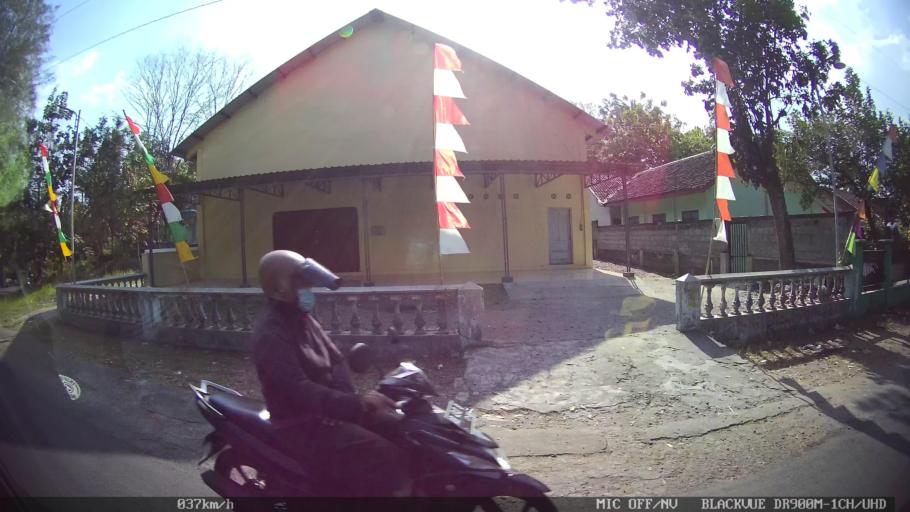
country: ID
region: Daerah Istimewa Yogyakarta
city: Kasihan
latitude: -7.8381
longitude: 110.3362
